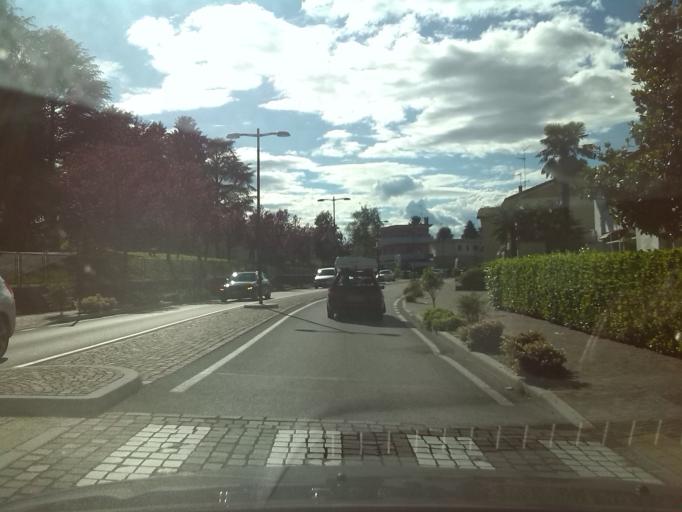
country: IT
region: Friuli Venezia Giulia
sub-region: Provincia di Udine
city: Tricesimo
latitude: 46.1594
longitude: 13.2128
